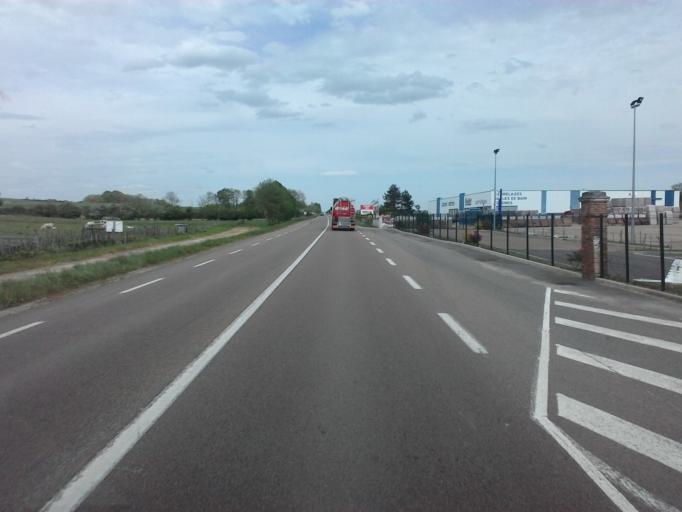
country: FR
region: Bourgogne
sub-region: Departement de l'Yonne
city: Saint-Florentin
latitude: 48.0112
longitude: 3.7516
